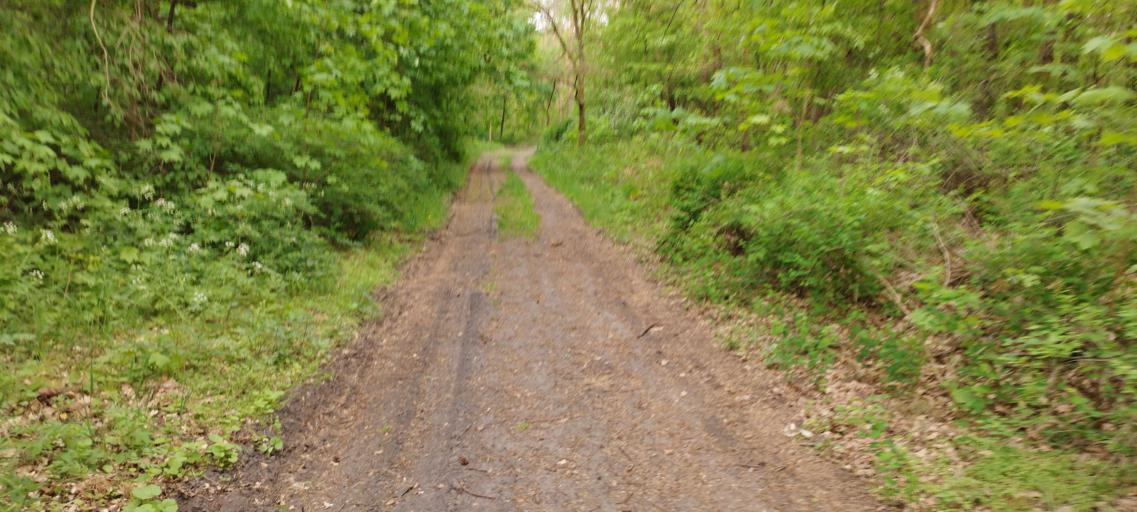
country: DE
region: Brandenburg
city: Rauen
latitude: 52.3615
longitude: 14.0231
